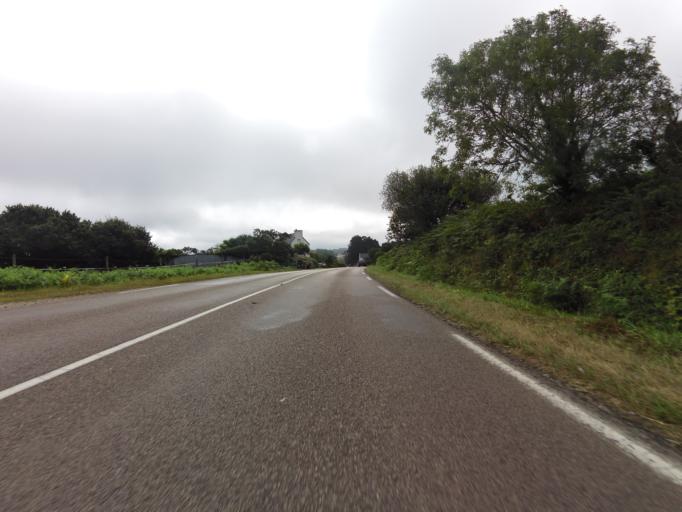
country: FR
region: Brittany
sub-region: Departement du Finistere
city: Plouhinec
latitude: 48.0112
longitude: -4.4645
